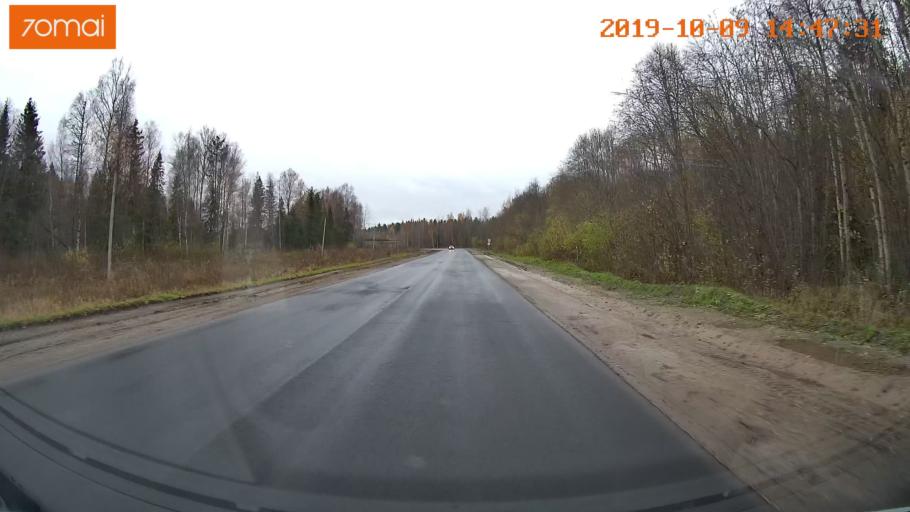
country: RU
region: Kostroma
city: Buy
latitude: 58.4170
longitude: 41.5722
